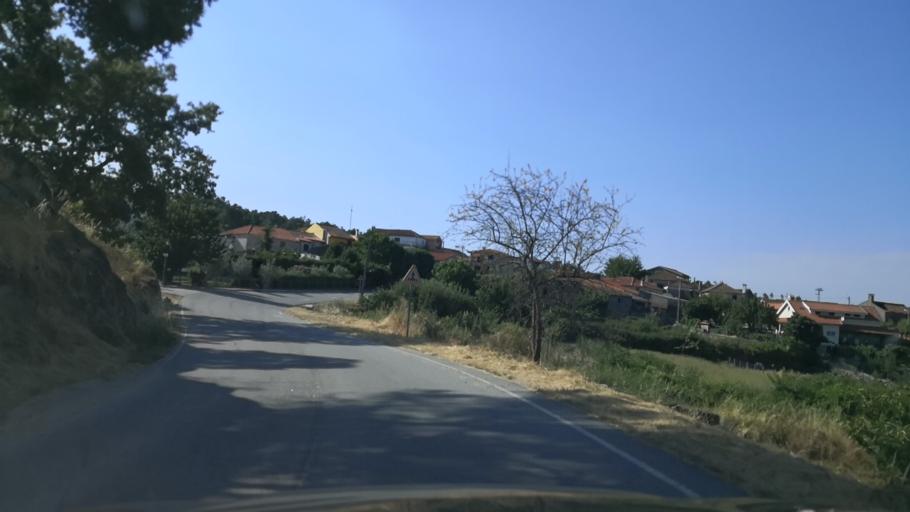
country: PT
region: Vila Real
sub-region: Murca
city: Murca
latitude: 41.3723
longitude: -7.5029
